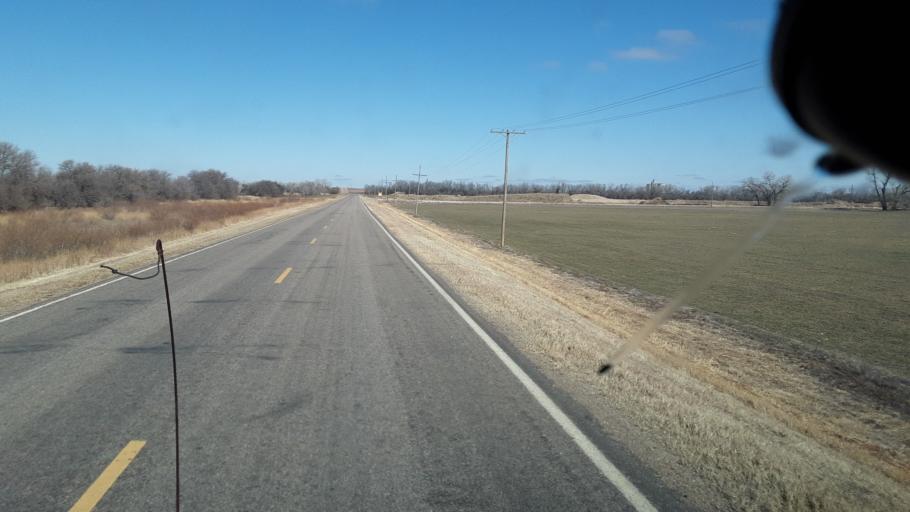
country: US
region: Kansas
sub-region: Barton County
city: Ellinwood
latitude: 38.3478
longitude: -98.6642
